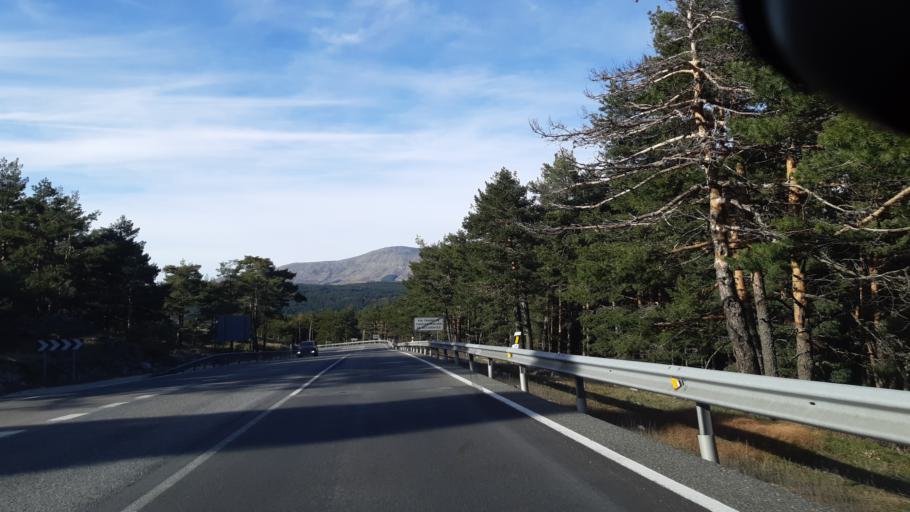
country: ES
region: Madrid
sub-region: Provincia de Madrid
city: Guadarrama
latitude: 40.7063
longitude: -4.1489
